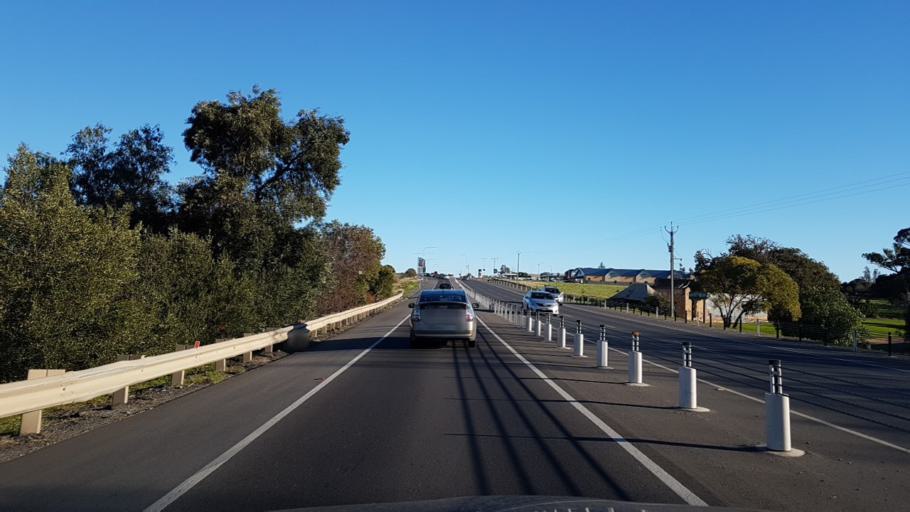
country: AU
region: South Australia
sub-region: Onkaparinga
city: Aldinga
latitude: -35.2645
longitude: 138.4873
